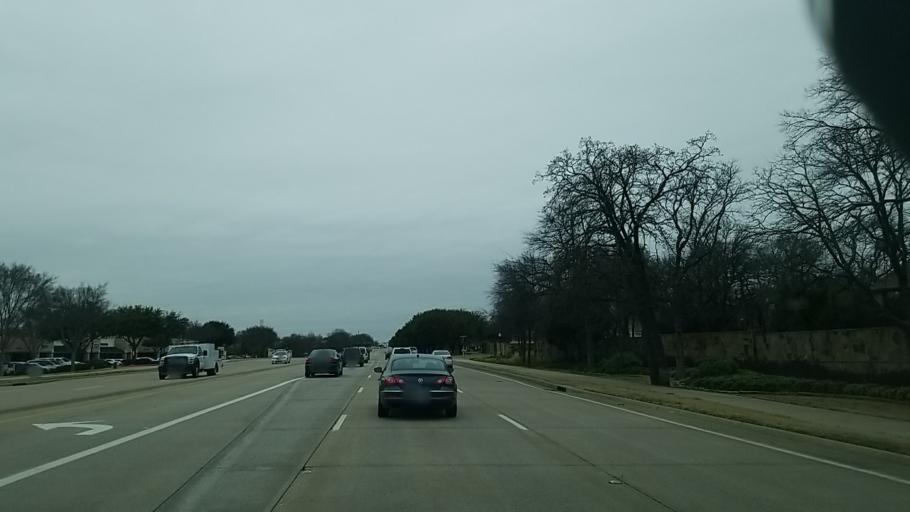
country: US
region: Texas
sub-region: Denton County
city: Flower Mound
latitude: 33.0224
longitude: -97.0709
